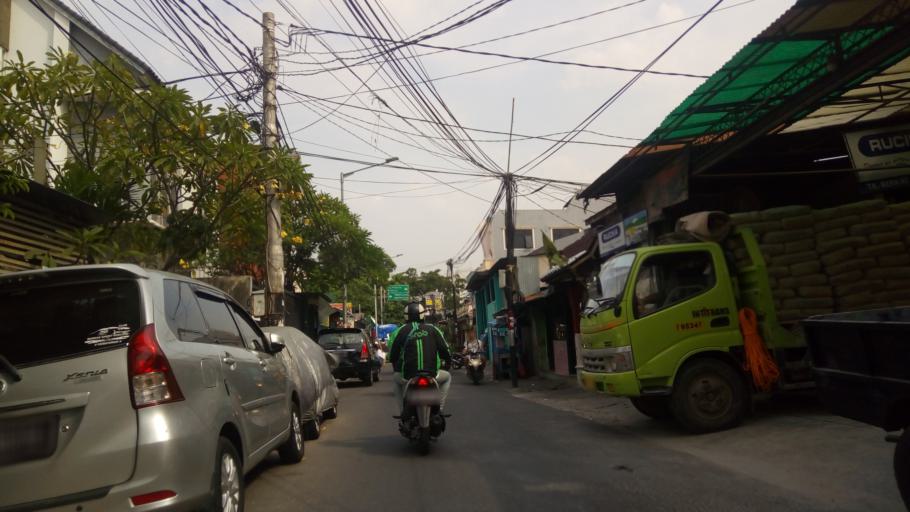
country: ID
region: Jakarta Raya
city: Jakarta
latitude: -6.1707
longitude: 106.8491
